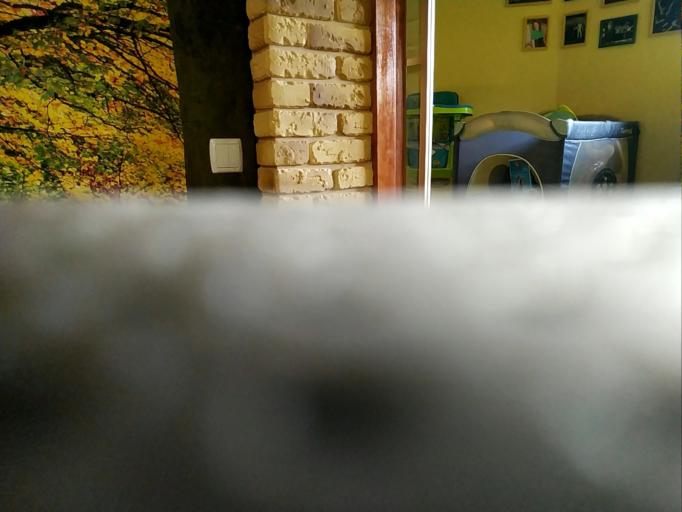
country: RU
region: Kaluga
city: Sukhinichi
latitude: 54.0898
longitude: 35.2833
